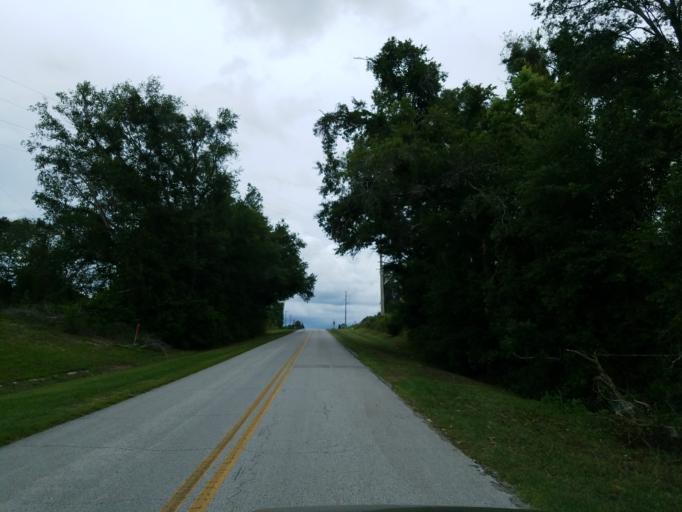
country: US
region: Florida
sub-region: Alachua County
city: High Springs
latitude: 29.9491
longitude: -82.5072
